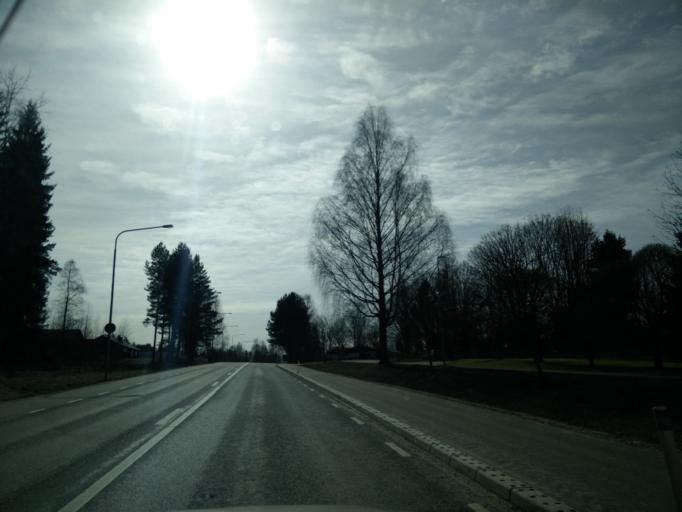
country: SE
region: Vaermland
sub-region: Hagfors Kommun
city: Hagfors
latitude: 60.0164
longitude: 13.6821
